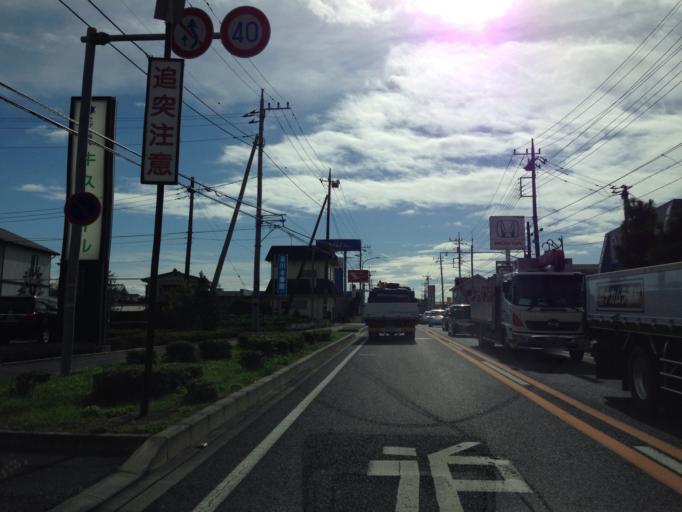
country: JP
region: Ibaraki
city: Ushiku
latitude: 35.9703
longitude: 140.1396
